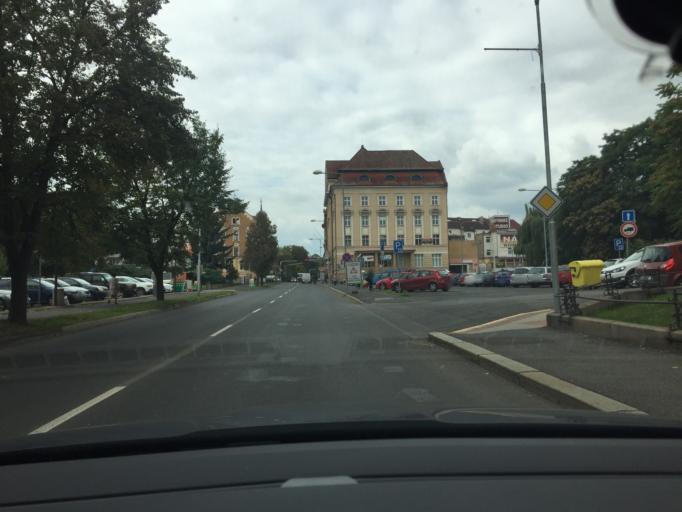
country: CZ
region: Ustecky
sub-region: Okres Litomerice
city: Litomerice
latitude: 50.5355
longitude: 14.1353
